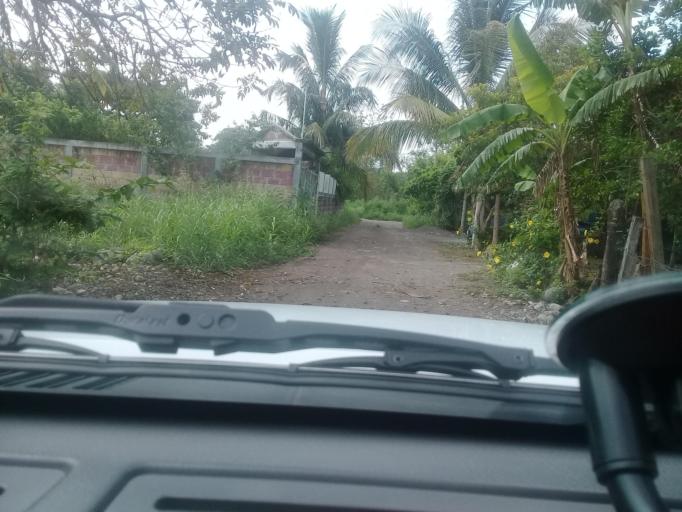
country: MX
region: Veracruz
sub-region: Paso de Ovejas
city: Tolome
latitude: 19.2699
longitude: -96.4005
